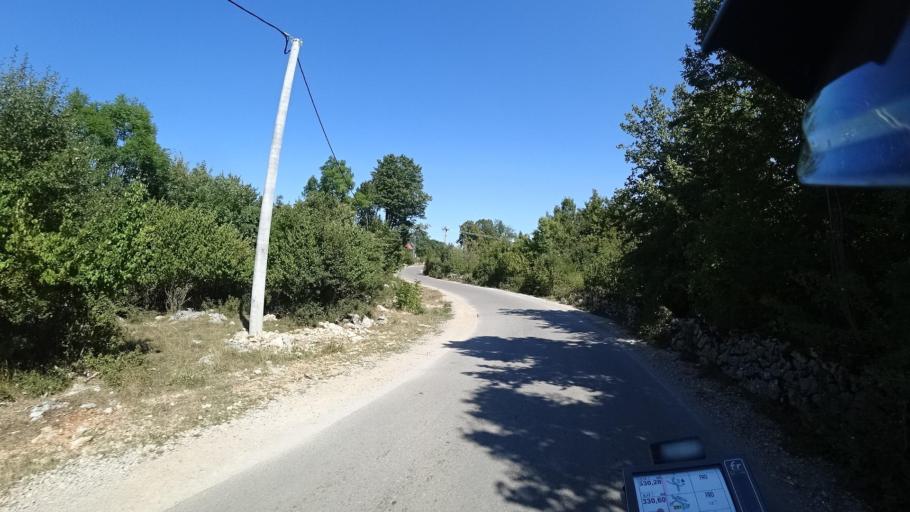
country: HR
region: Licko-Senjska
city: Otocac
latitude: 44.7291
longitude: 15.3173
